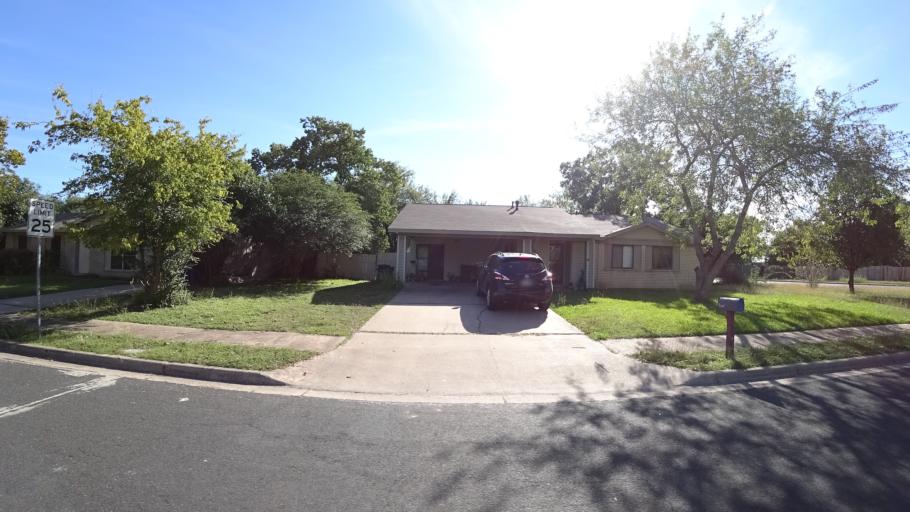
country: US
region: Texas
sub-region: Travis County
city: Onion Creek
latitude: 30.1868
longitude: -97.7458
